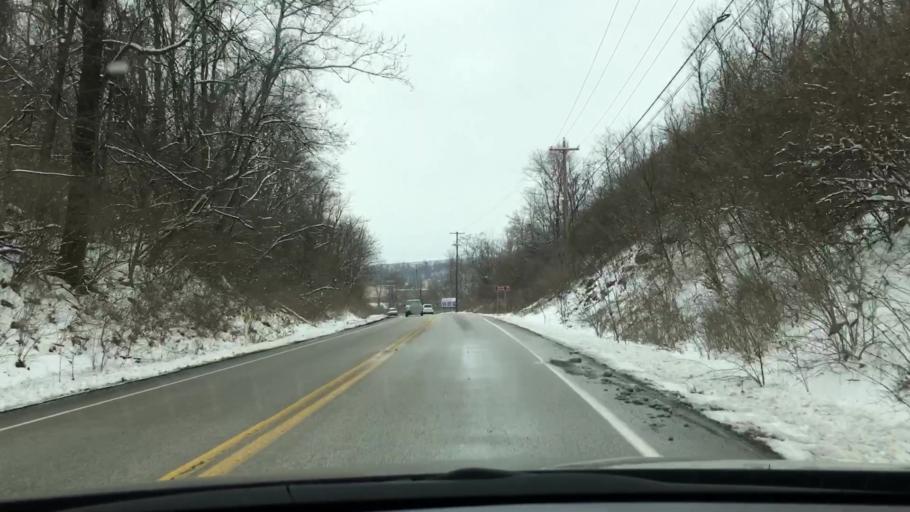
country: US
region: Pennsylvania
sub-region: York County
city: Emigsville
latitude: 40.0150
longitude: -76.7182
